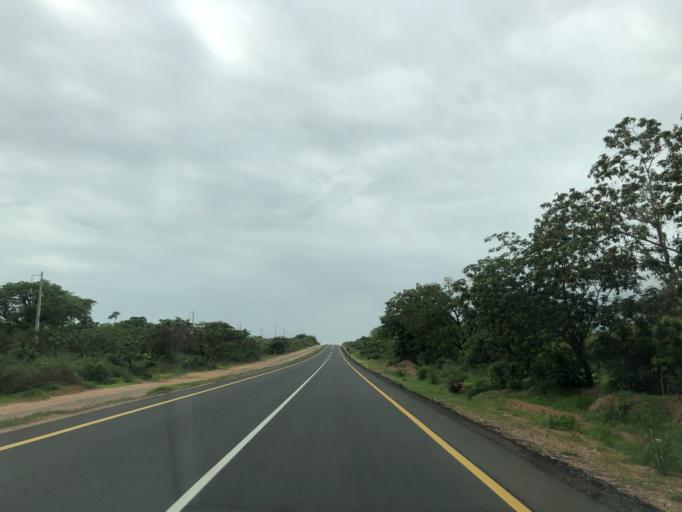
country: AO
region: Cuanza Norte
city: N'dalatando
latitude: -9.4334
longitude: 14.3084
